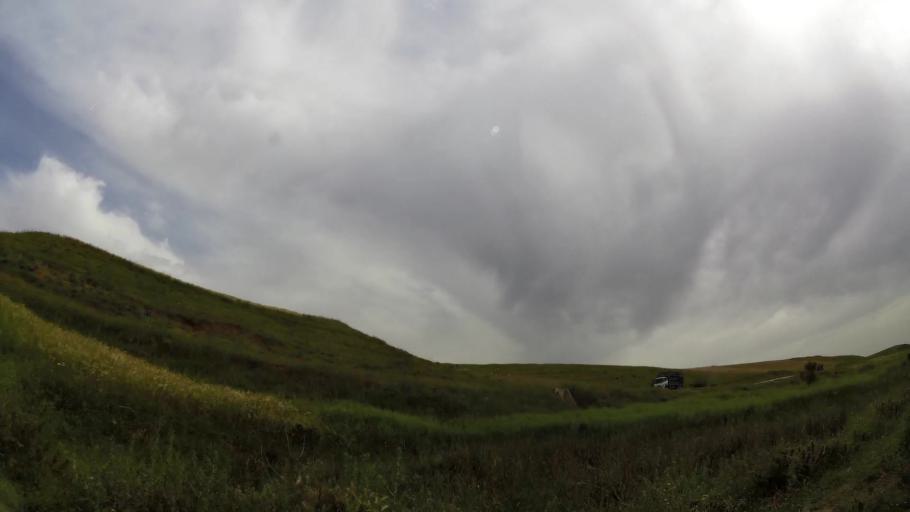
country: MA
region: Rabat-Sale-Zemmour-Zaer
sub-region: Khemisset
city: Khemisset
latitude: 33.7585
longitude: -6.2126
